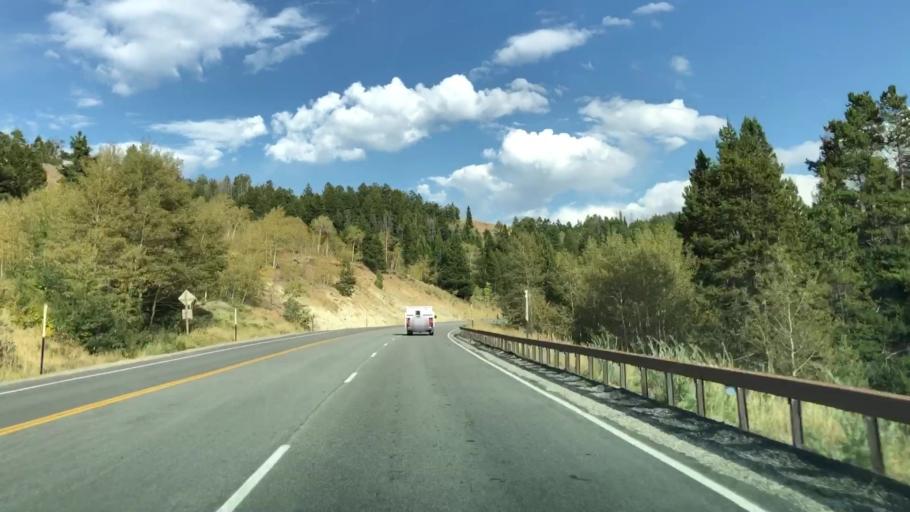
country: US
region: Wyoming
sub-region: Sublette County
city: Pinedale
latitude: 43.1383
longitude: -110.2124
